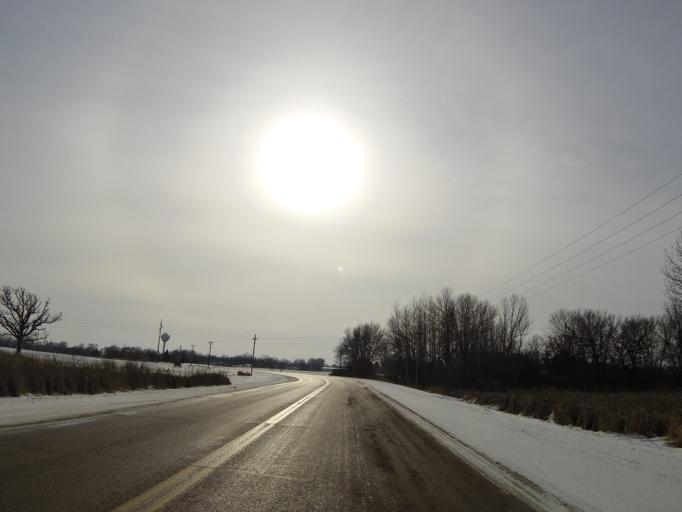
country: US
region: Minnesota
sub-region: McLeod County
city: Lester Prairie
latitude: 44.8933
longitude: -93.9714
